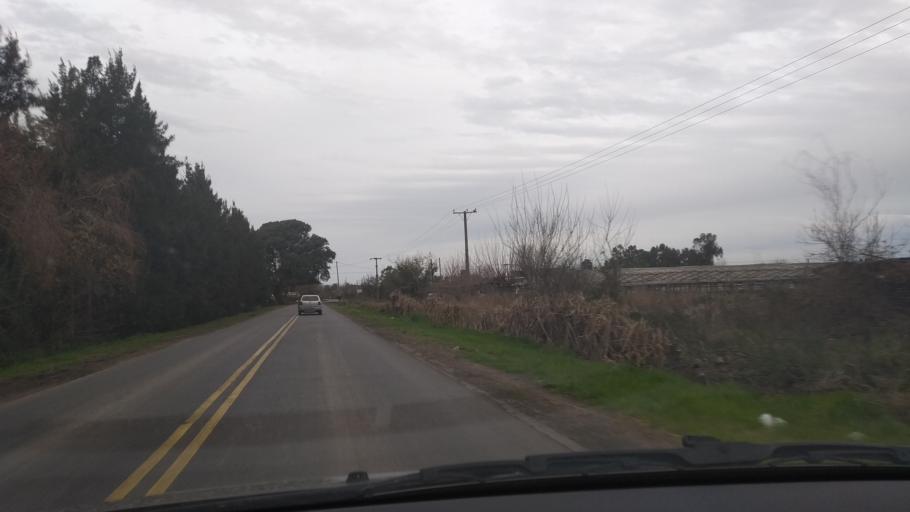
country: AR
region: Buenos Aires
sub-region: Partido de La Plata
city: La Plata
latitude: -34.9997
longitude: -58.0681
